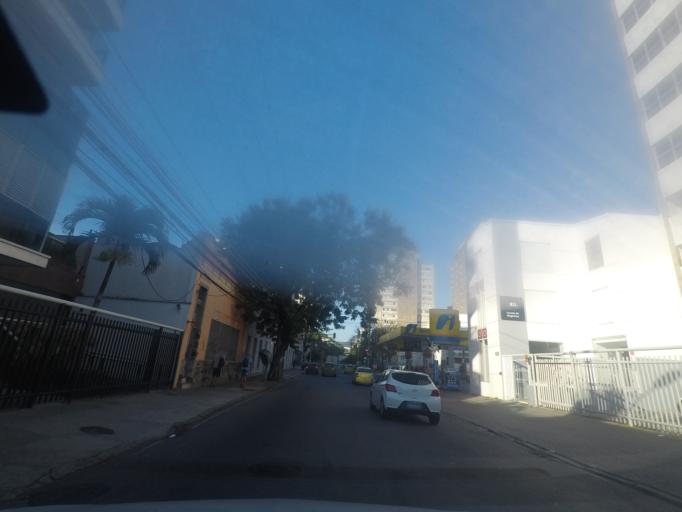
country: BR
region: Rio de Janeiro
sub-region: Rio De Janeiro
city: Rio de Janeiro
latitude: -22.9553
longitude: -43.1896
